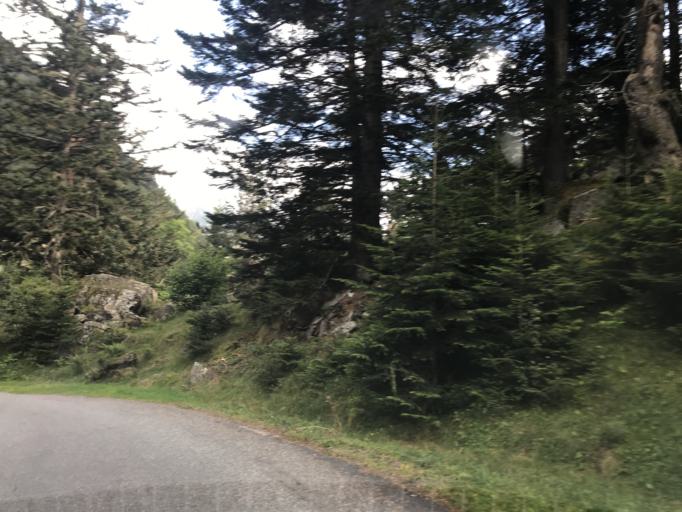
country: FR
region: Midi-Pyrenees
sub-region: Departement des Hautes-Pyrenees
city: Saint-Lary-Soulan
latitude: 42.8180
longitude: 0.1934
